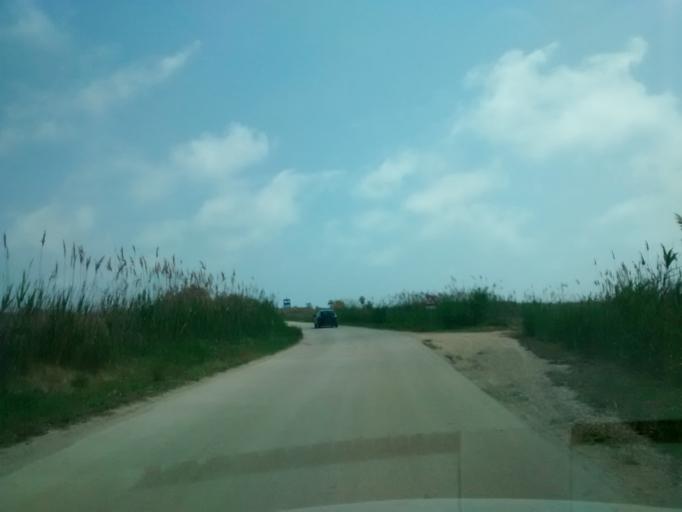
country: ES
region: Catalonia
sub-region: Provincia de Tarragona
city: Deltebre
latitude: 40.6898
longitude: 0.8454
